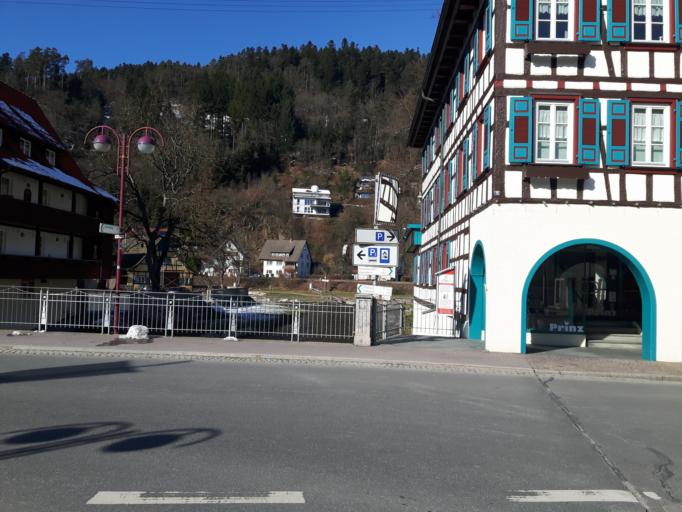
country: DE
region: Baden-Wuerttemberg
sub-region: Freiburg Region
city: Schiltach
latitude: 48.2902
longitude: 8.3424
